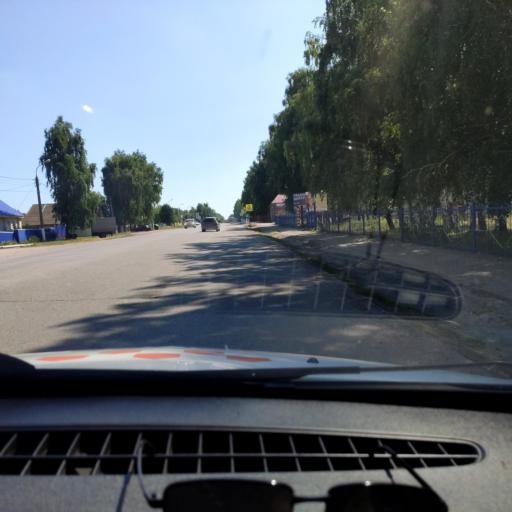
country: RU
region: Bashkortostan
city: Tolbazy
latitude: 54.0180
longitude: 55.8864
